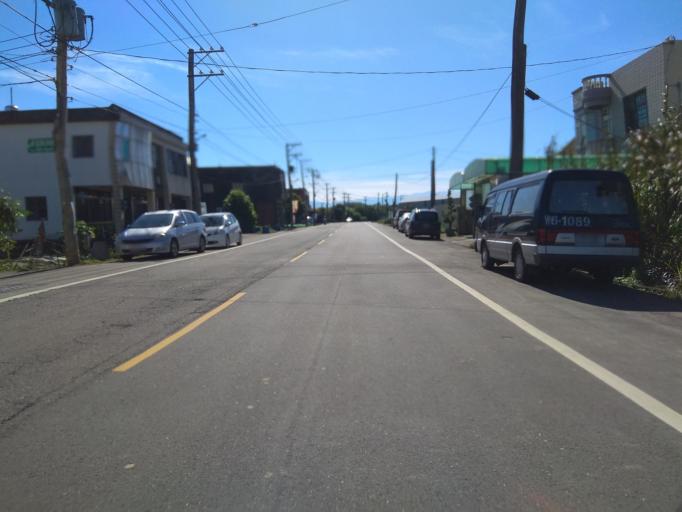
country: TW
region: Taiwan
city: Taoyuan City
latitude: 24.9814
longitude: 121.1359
